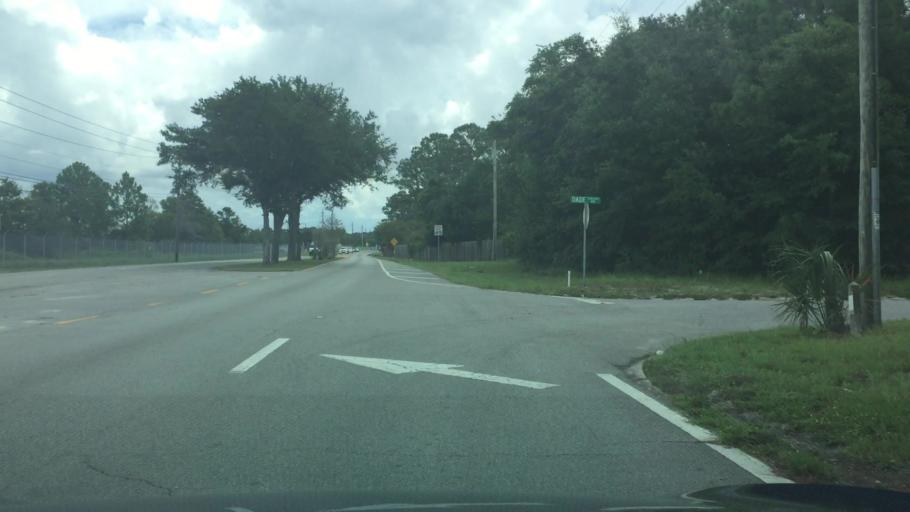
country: US
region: Florida
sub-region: Bay County
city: Upper Grand Lagoon
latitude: 30.1587
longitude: -85.7467
